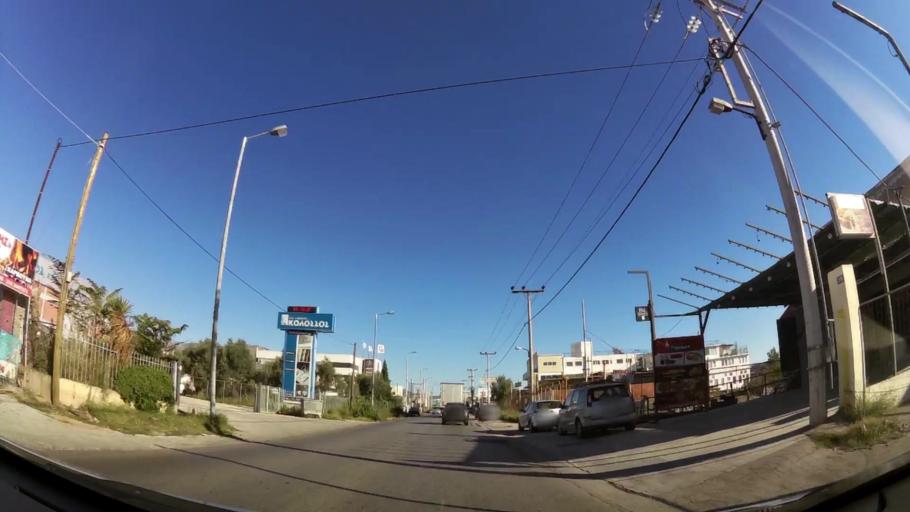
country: GR
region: Attica
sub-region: Nomarchia Athinas
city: Metamorfosi
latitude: 38.0817
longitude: 23.7629
